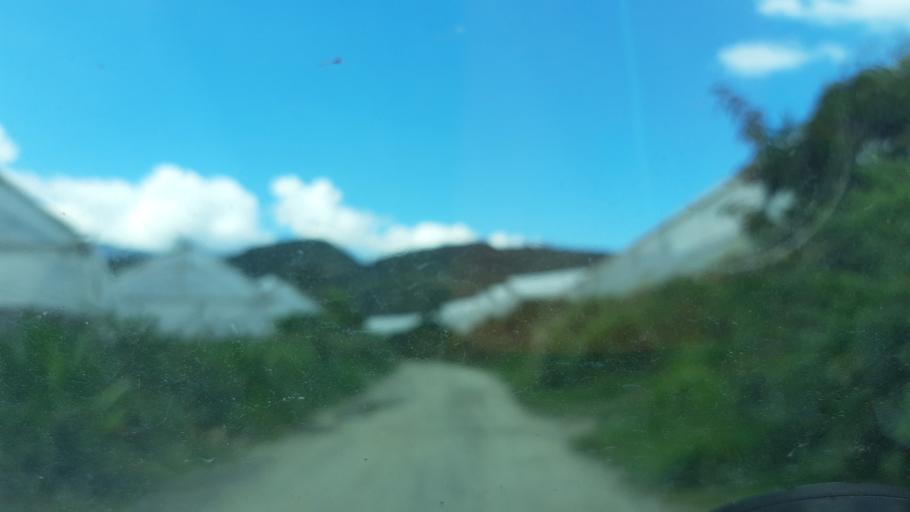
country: CO
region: Boyaca
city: Santa Sofia
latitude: 5.6900
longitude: -73.5702
